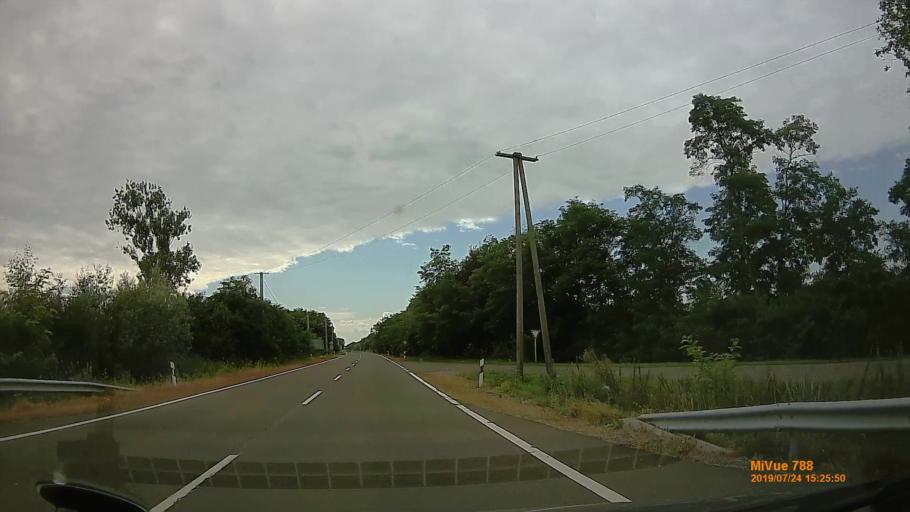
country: HU
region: Szabolcs-Szatmar-Bereg
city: Tarpa
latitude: 48.1598
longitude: 22.5355
